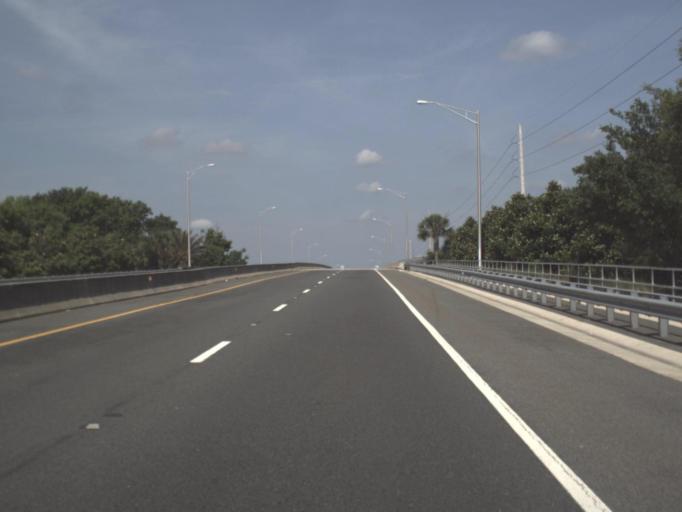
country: US
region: Florida
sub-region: Duval County
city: Atlantic Beach
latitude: 30.3588
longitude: -81.4559
